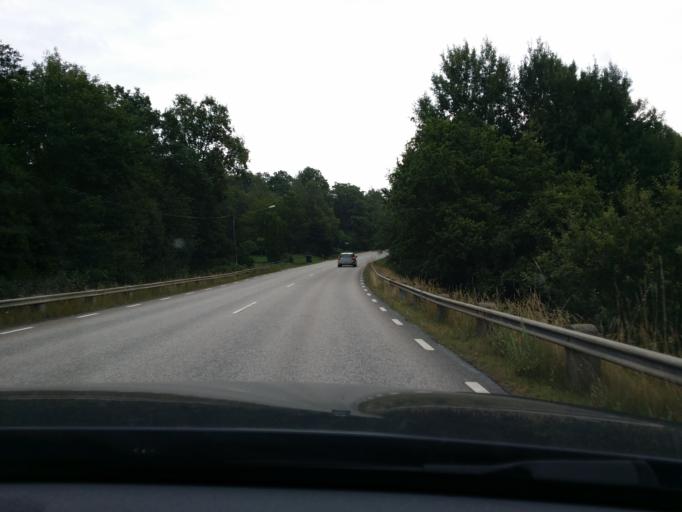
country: SE
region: Blekinge
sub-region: Karlshamns Kommun
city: Morrum
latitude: 56.1859
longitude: 14.7666
